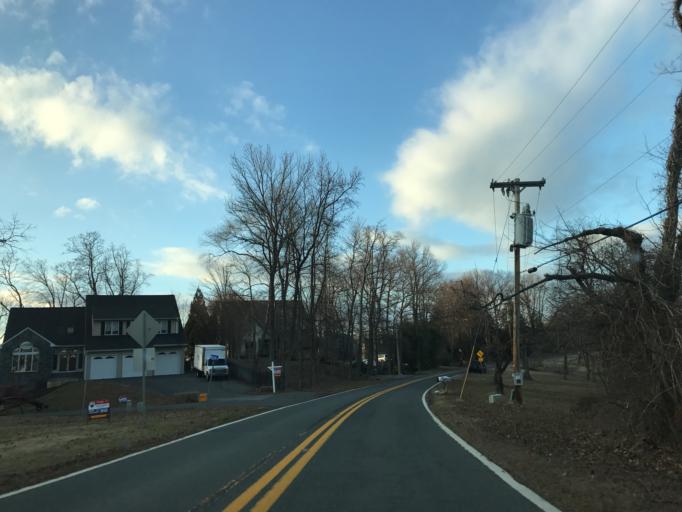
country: US
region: Maryland
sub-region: Cecil County
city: Charlestown
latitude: 39.4655
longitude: -75.9958
